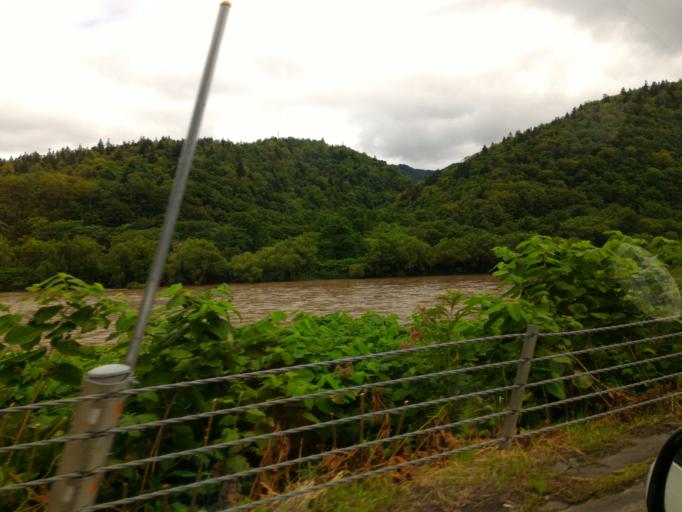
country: JP
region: Hokkaido
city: Nayoro
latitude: 44.7347
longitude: 142.1442
